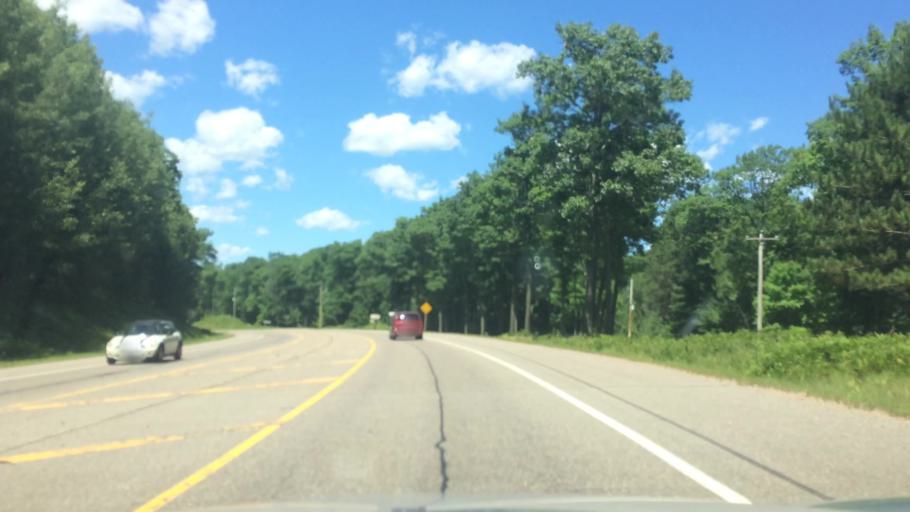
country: US
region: Wisconsin
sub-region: Vilas County
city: Lac du Flambeau
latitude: 45.7886
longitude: -89.7101
